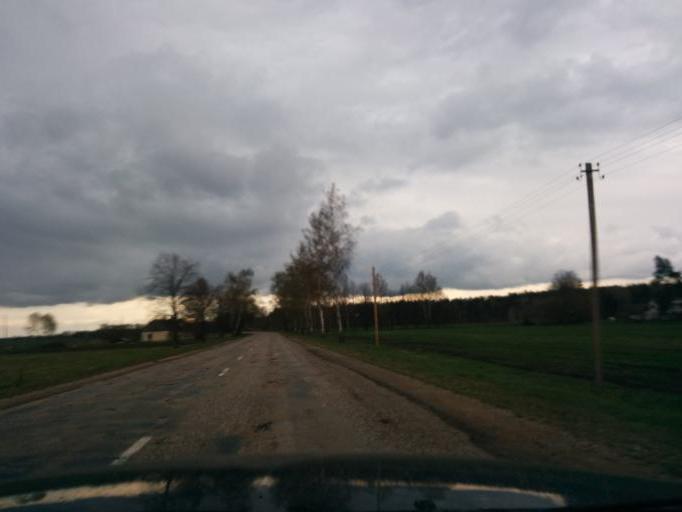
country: LT
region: Siauliu apskritis
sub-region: Joniskis
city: Joniskis
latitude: 56.4180
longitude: 23.5790
